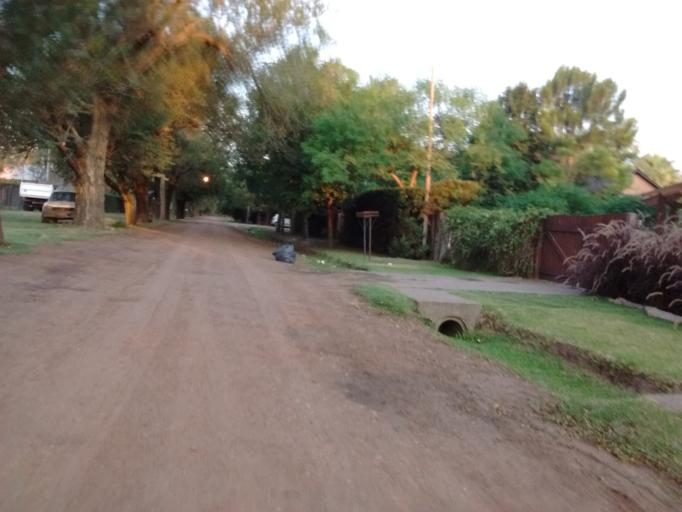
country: AR
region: Santa Fe
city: Funes
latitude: -32.9232
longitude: -60.8412
